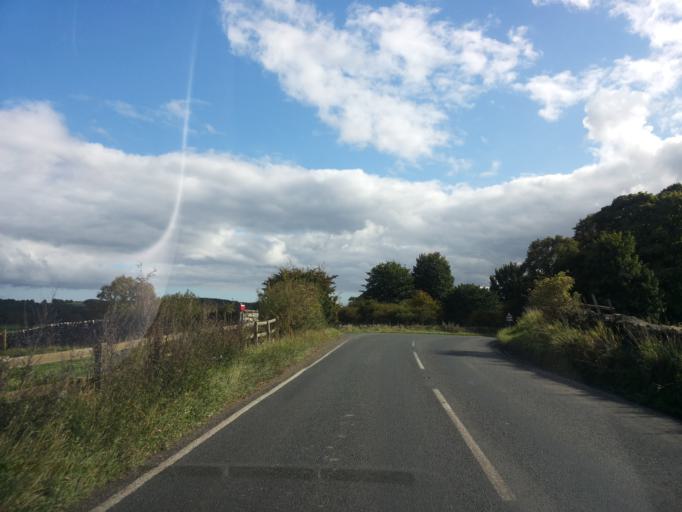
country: GB
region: England
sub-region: North Yorkshire
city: Leyburn
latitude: 54.2923
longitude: -1.8156
